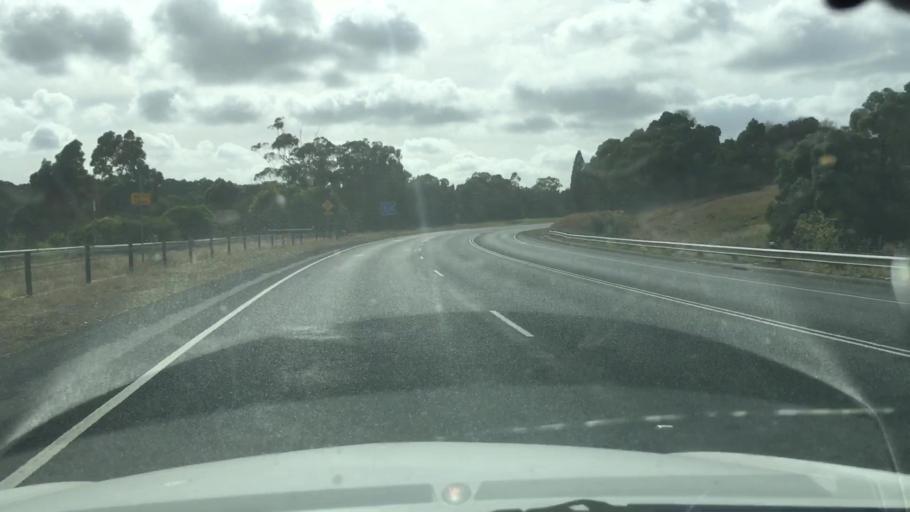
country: AU
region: Victoria
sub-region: Yarra Ranges
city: Selby
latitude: -37.9368
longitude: 145.3875
